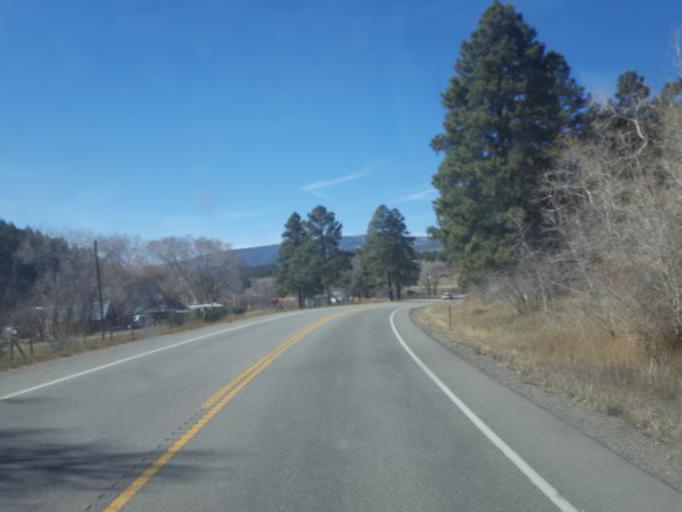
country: US
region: Colorado
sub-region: Archuleta County
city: Pagosa Springs
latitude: 37.2388
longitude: -107.1370
